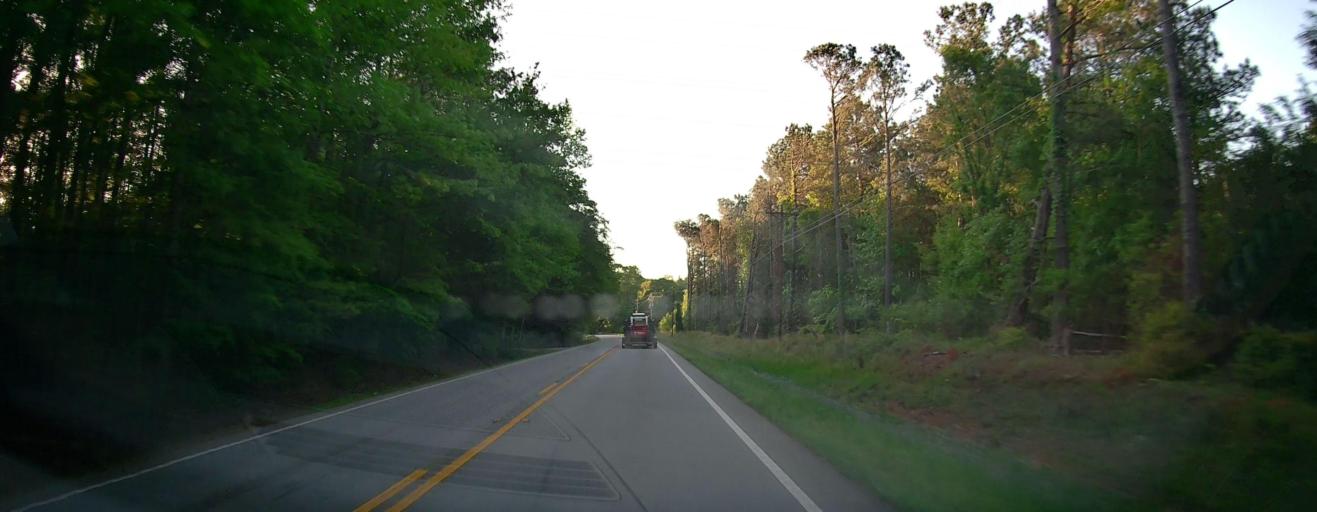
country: US
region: Georgia
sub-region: Walton County
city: Social Circle
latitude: 33.5426
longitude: -83.7274
